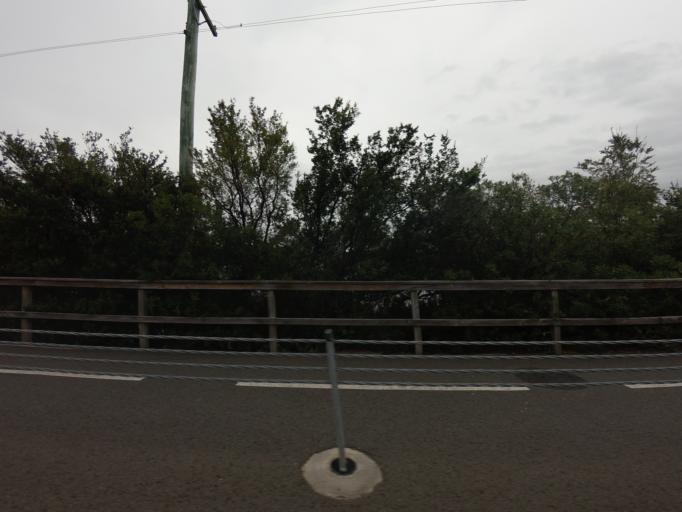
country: AU
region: Tasmania
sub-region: Clarence
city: Bellerive
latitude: -42.8807
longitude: 147.3697
